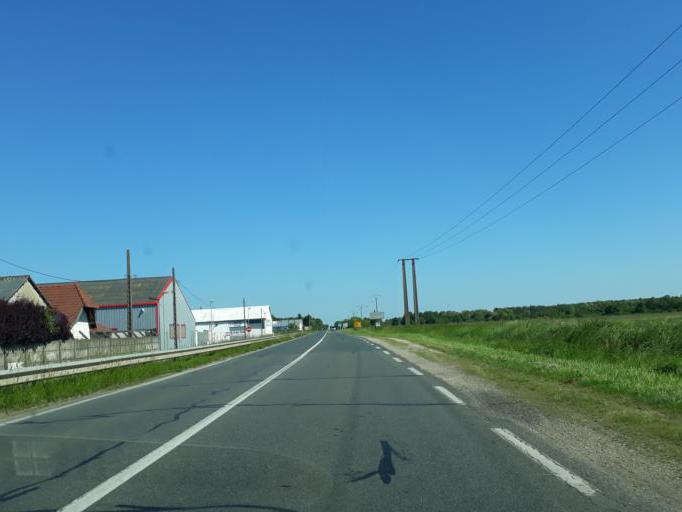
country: FR
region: Centre
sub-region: Departement du Loiret
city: Briare
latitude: 47.6120
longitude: 2.7709
